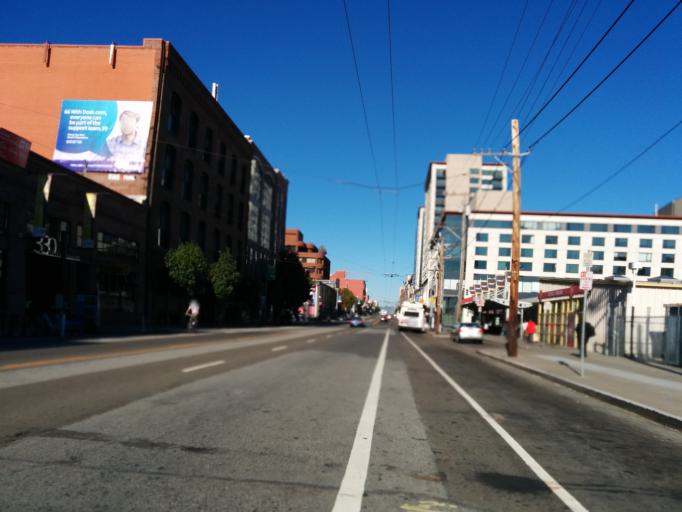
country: US
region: California
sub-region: San Francisco County
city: San Francisco
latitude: 37.7764
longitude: -122.3959
